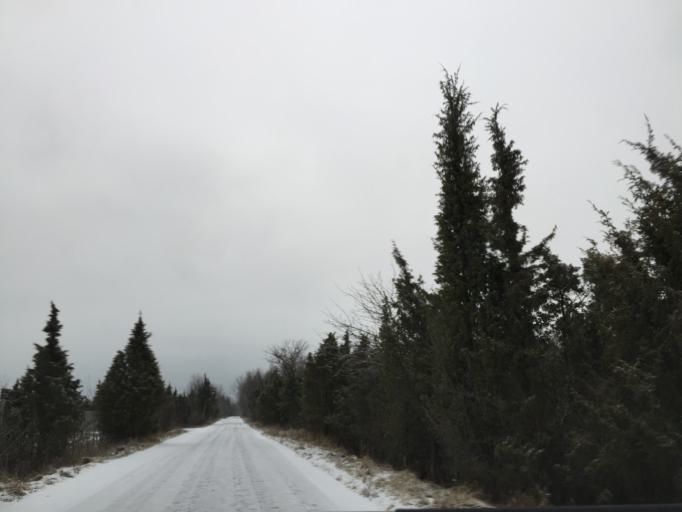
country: EE
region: Saare
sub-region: Orissaare vald
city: Orissaare
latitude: 58.5533
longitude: 23.3895
